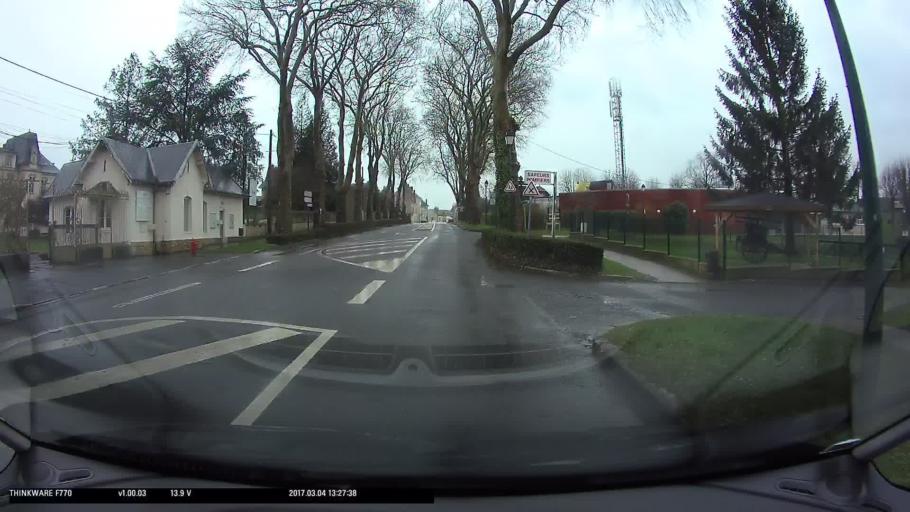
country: FR
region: Ile-de-France
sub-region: Departement du Val-d'Oise
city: Marines
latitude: 49.1468
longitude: 1.9748
